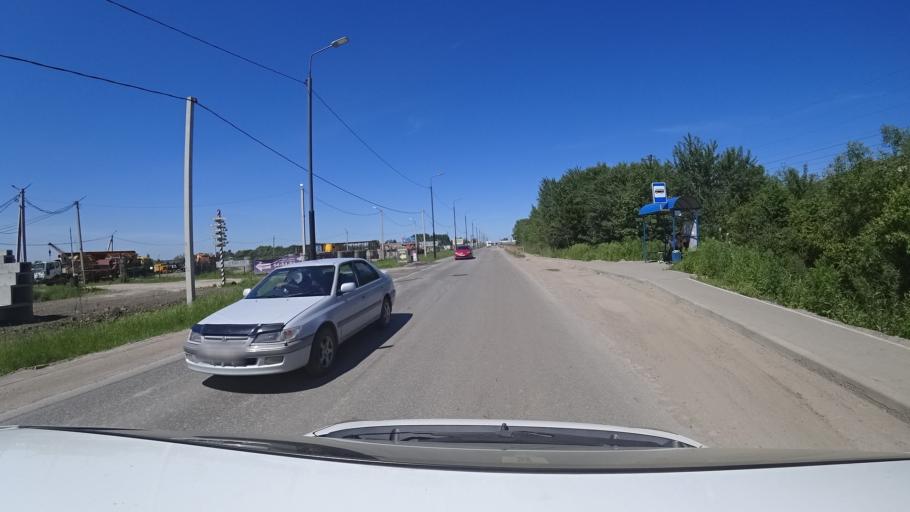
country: RU
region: Khabarovsk Krai
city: Topolevo
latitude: 48.4911
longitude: 135.1843
